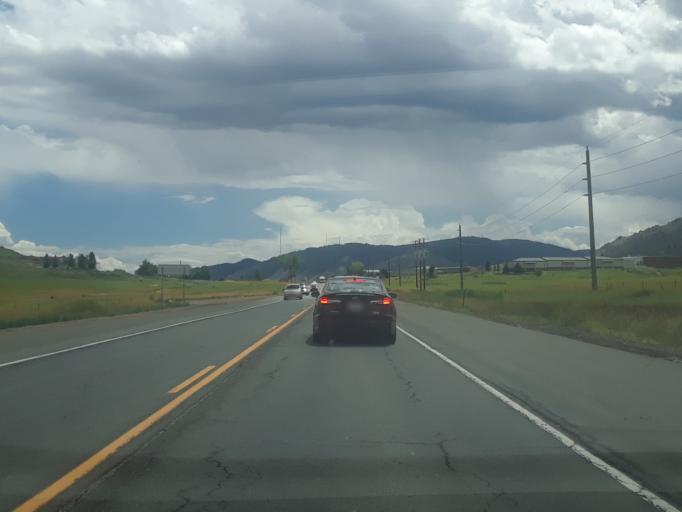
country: US
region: Colorado
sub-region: Jefferson County
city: Golden
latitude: 39.7864
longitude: -105.2310
